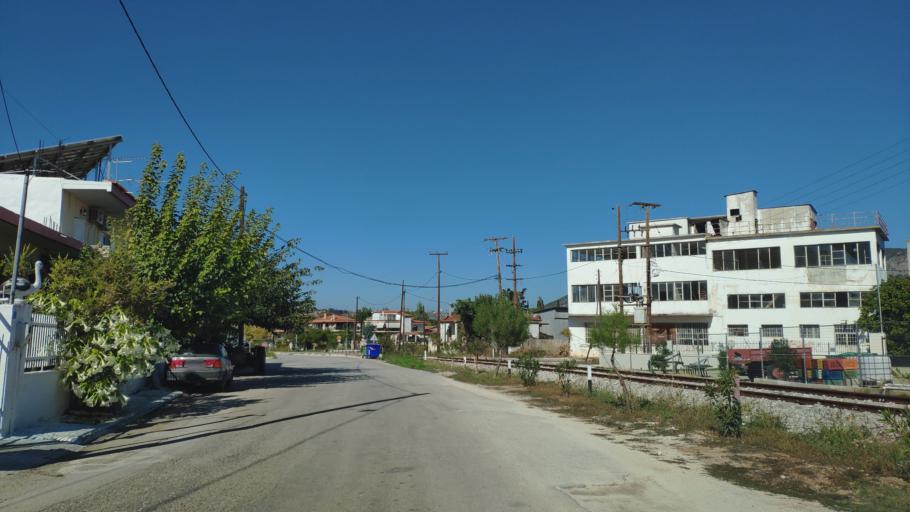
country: GR
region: Peloponnese
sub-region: Nomos Korinthias
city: Khiliomodhi
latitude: 37.8074
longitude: 22.8671
